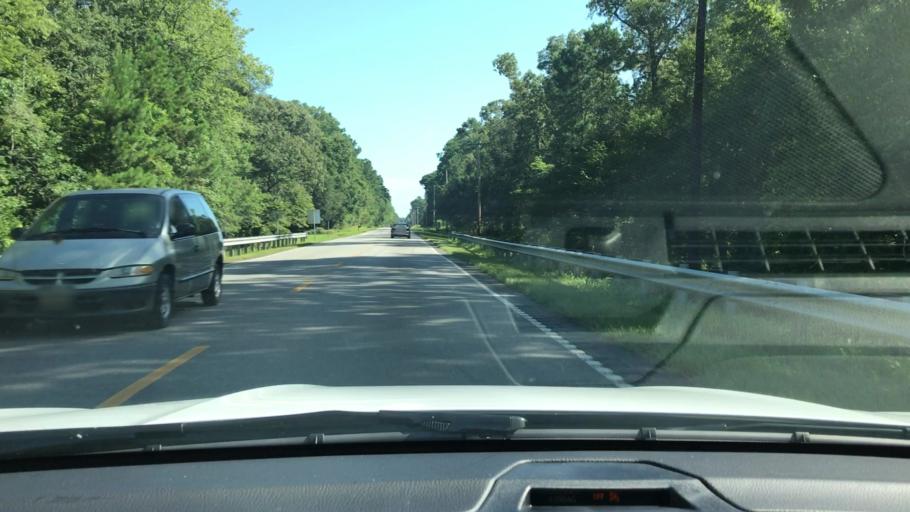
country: US
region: South Carolina
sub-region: Horry County
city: Conway
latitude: 33.7504
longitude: -79.0777
